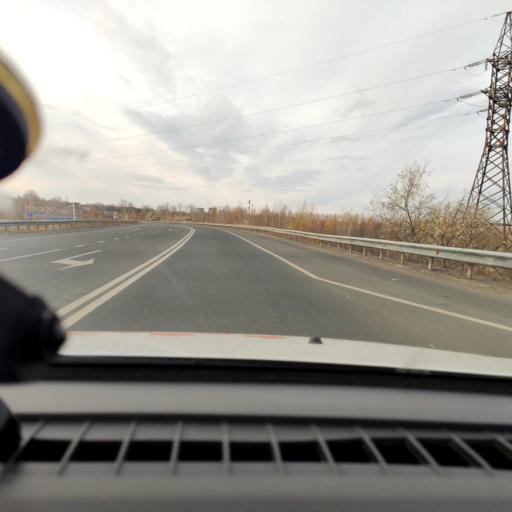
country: RU
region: Samara
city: Novokuybyshevsk
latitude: 53.1274
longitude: 49.9486
